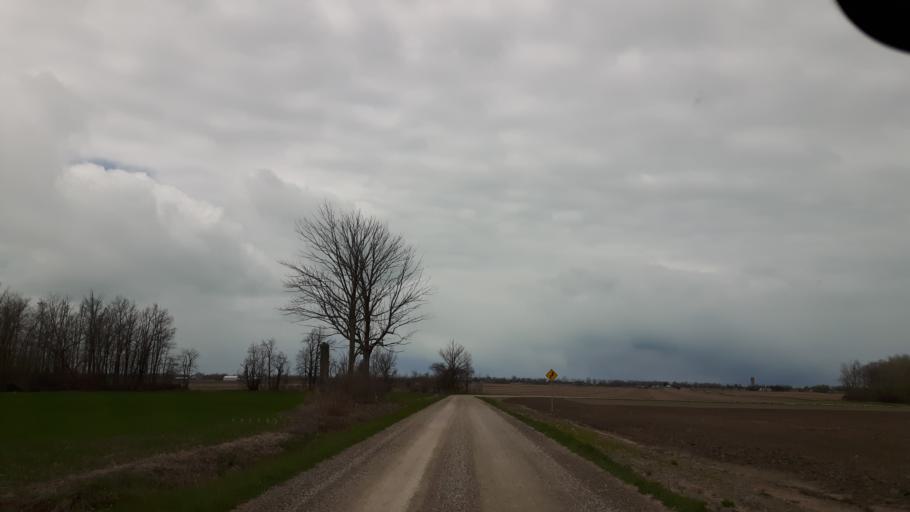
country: CA
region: Ontario
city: Bluewater
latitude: 43.4710
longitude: -81.6780
